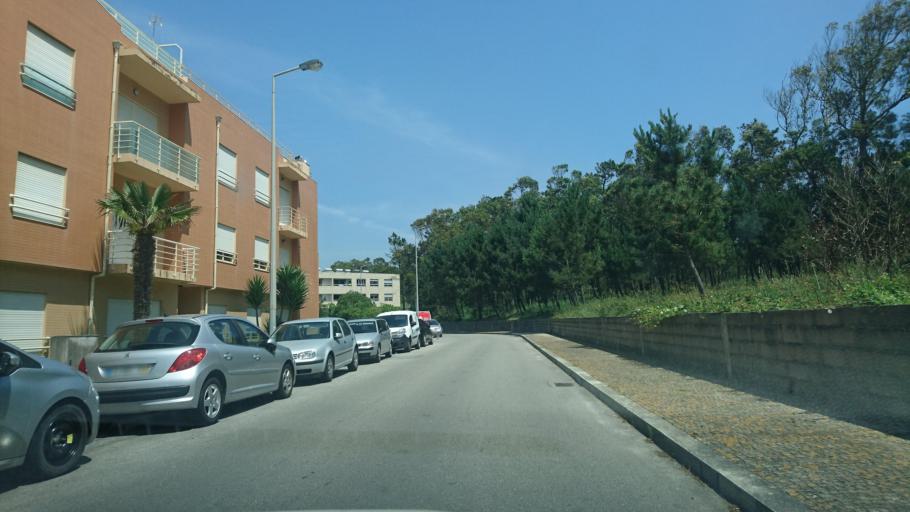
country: PT
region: Porto
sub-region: Matosinhos
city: Lavra
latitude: 41.2725
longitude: -8.7230
